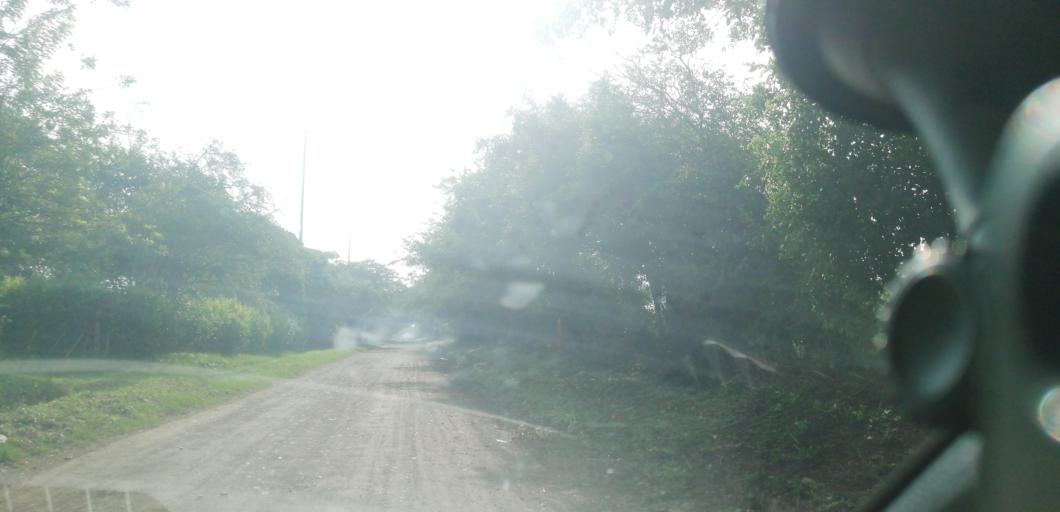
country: CO
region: Valle del Cauca
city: Yumbo
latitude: 3.5811
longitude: -76.4199
